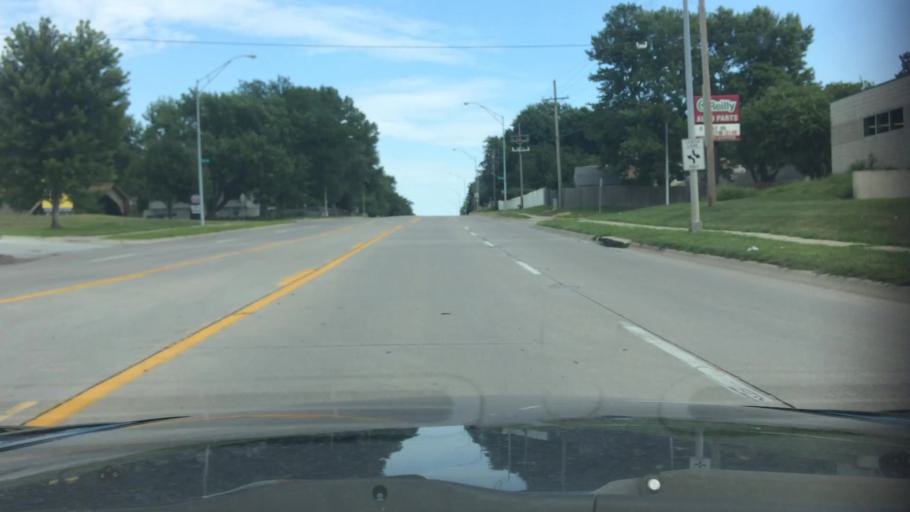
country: US
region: Nebraska
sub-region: Douglas County
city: Ralston
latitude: 41.2053
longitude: -96.0799
